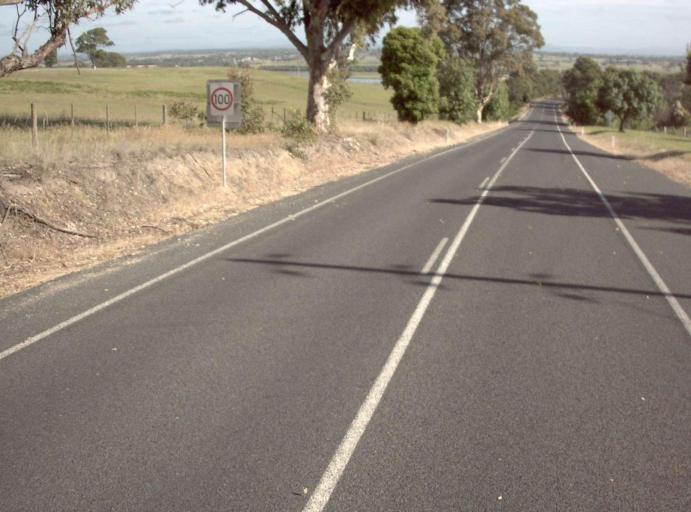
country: AU
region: Victoria
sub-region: East Gippsland
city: Lakes Entrance
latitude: -37.8572
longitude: 147.8453
